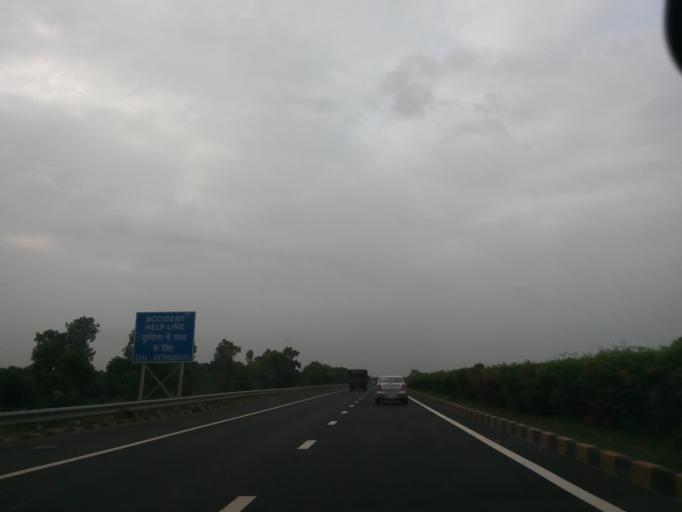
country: IN
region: Gujarat
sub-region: Kheda
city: Chaklasi
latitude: 22.6587
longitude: 72.9233
